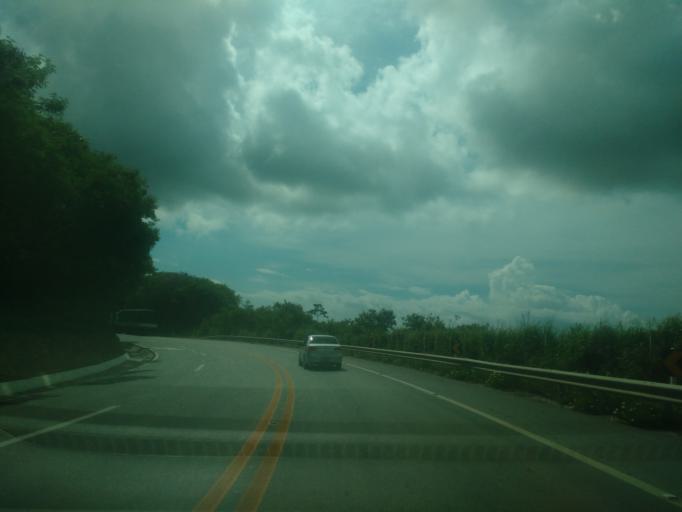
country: BR
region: Alagoas
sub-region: Marechal Deodoro
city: Marechal Deodoro
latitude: -9.6863
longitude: -35.8252
